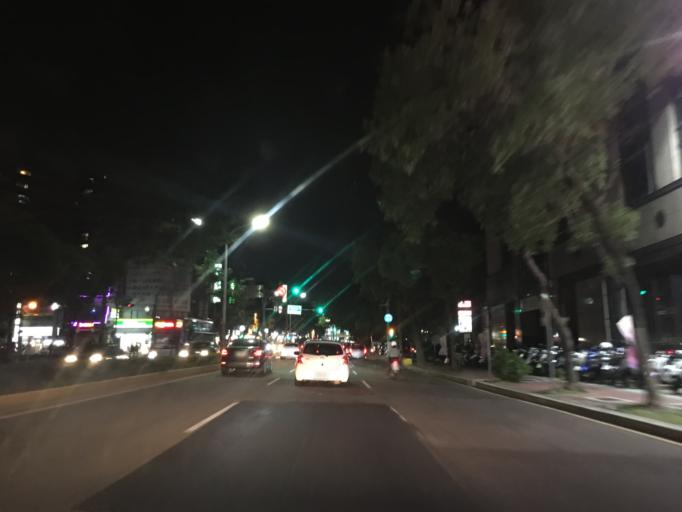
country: TW
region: Taiwan
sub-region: Hsinchu
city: Hsinchu
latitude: 24.7977
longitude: 120.9951
